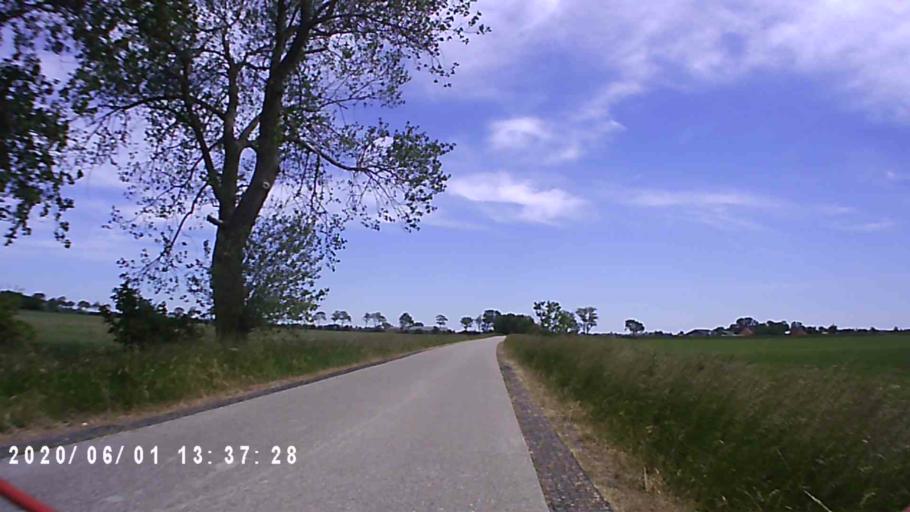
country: NL
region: Friesland
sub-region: Gemeente Littenseradiel
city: Wommels
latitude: 53.0856
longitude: 5.5945
